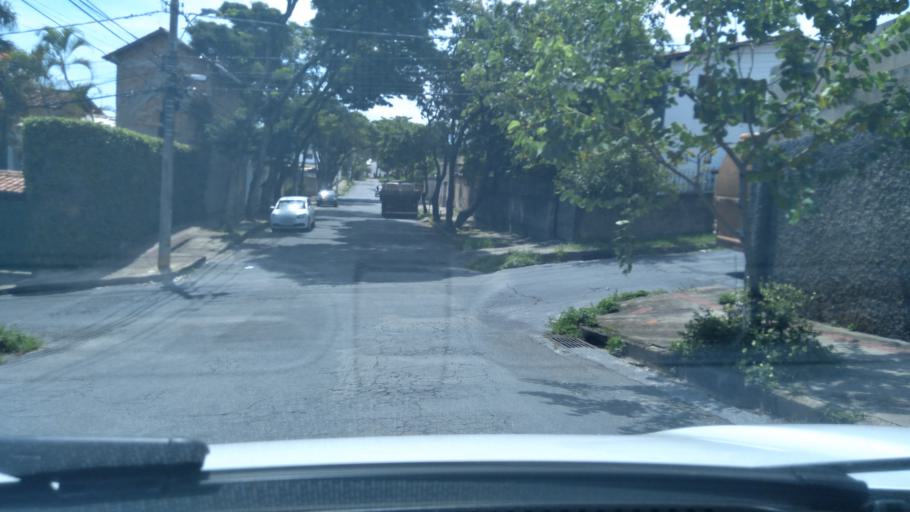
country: BR
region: Minas Gerais
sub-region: Contagem
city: Contagem
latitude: -19.9262
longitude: -44.0030
